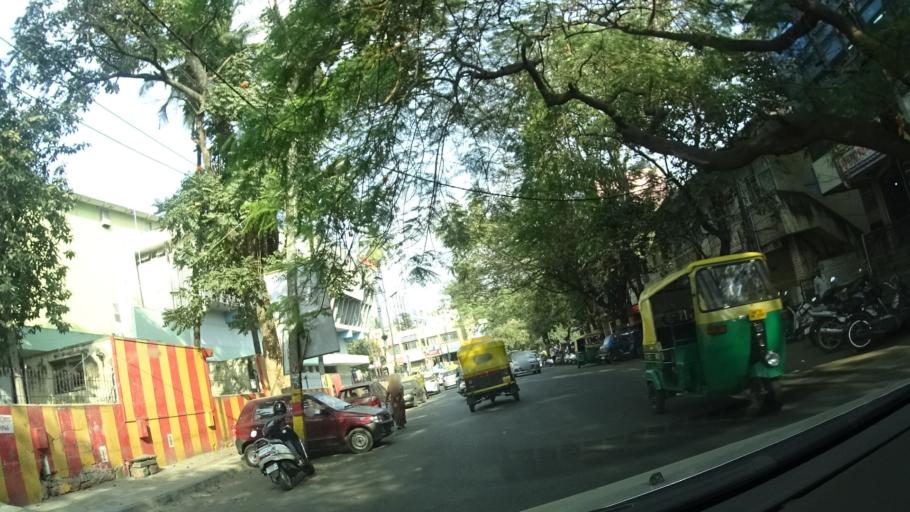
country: IN
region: Karnataka
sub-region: Bangalore Urban
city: Bangalore
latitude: 12.9551
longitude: 77.5667
